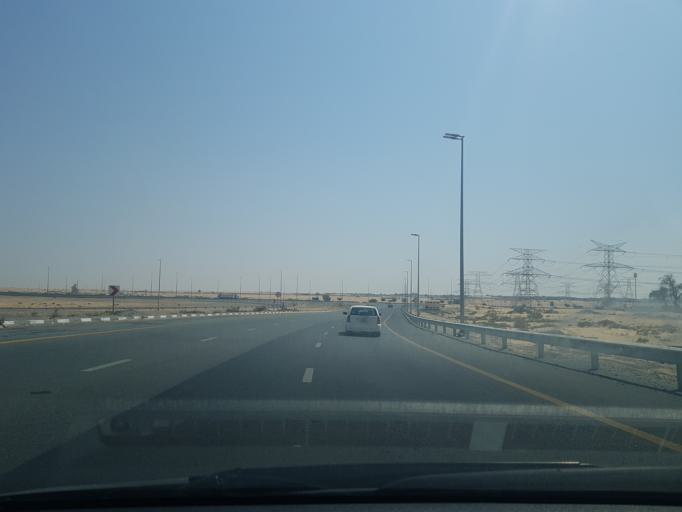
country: AE
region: Ash Shariqah
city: Sharjah
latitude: 25.2390
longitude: 55.5626
